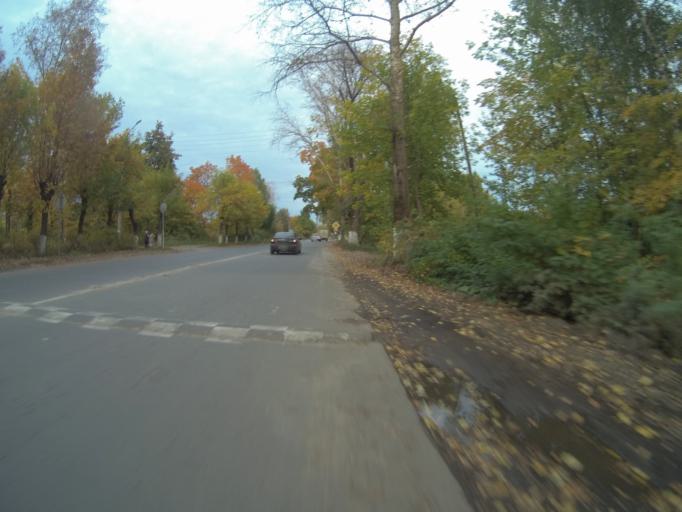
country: RU
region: Vladimir
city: Sobinka
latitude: 55.9953
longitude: 40.0217
